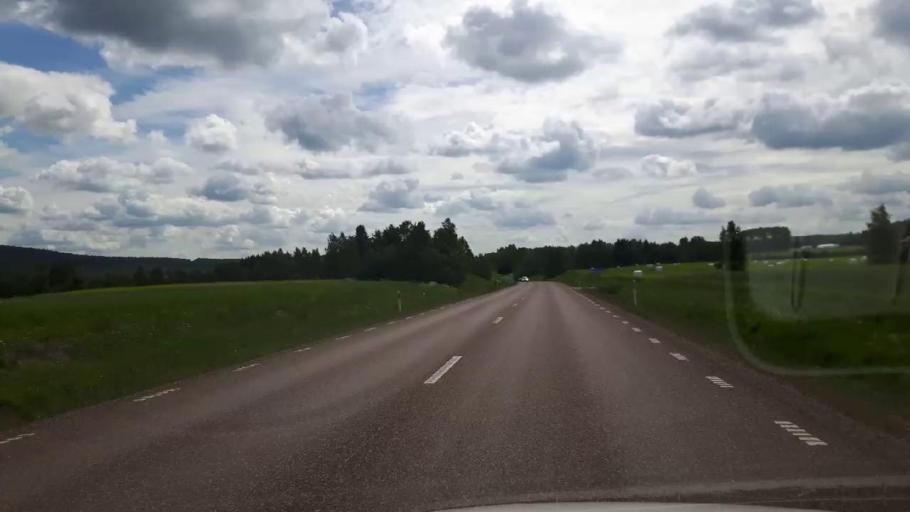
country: SE
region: Dalarna
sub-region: Hedemora Kommun
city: Langshyttan
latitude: 60.3861
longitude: 15.9049
